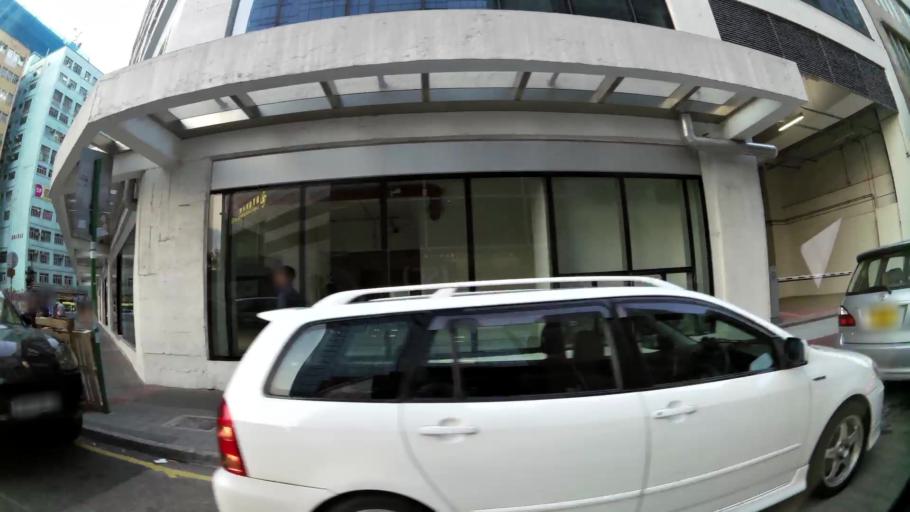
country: HK
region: Kowloon City
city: Kowloon
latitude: 22.3137
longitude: 114.2176
